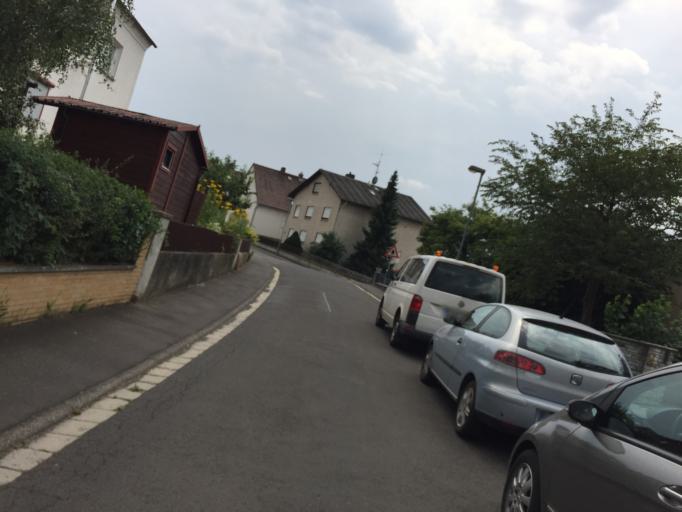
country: DE
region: Hesse
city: Staufenberg
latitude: 50.6611
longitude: 8.7227
